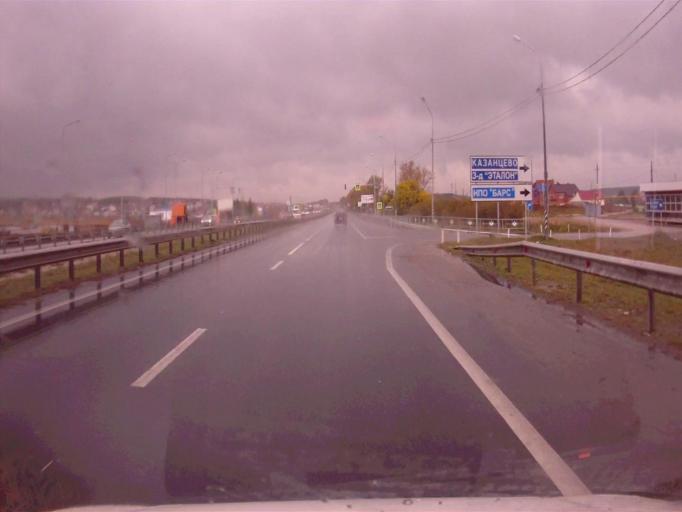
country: RU
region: Chelyabinsk
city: Dolgoderevenskoye
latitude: 55.2732
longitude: 61.3448
